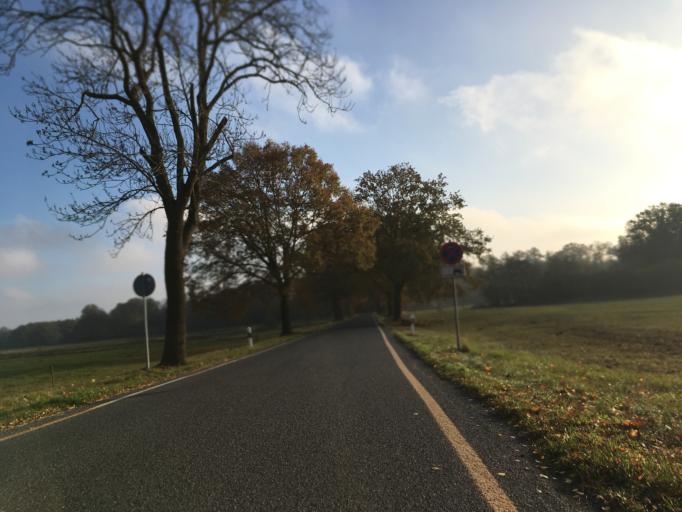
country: DE
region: Brandenburg
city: Schlepzig
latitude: 52.0344
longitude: 13.8515
